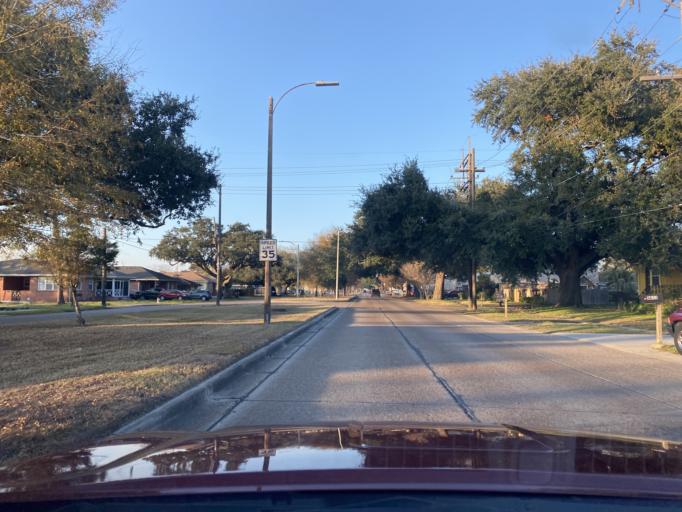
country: US
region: Louisiana
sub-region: Orleans Parish
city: New Orleans
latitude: 30.0190
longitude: -90.0515
